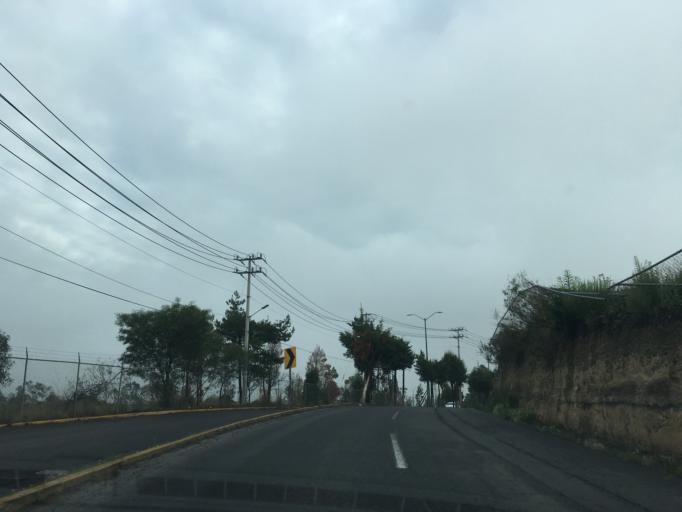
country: MX
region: Mexico
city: Ciudad Lopez Mateos
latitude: 19.5403
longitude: -99.2650
